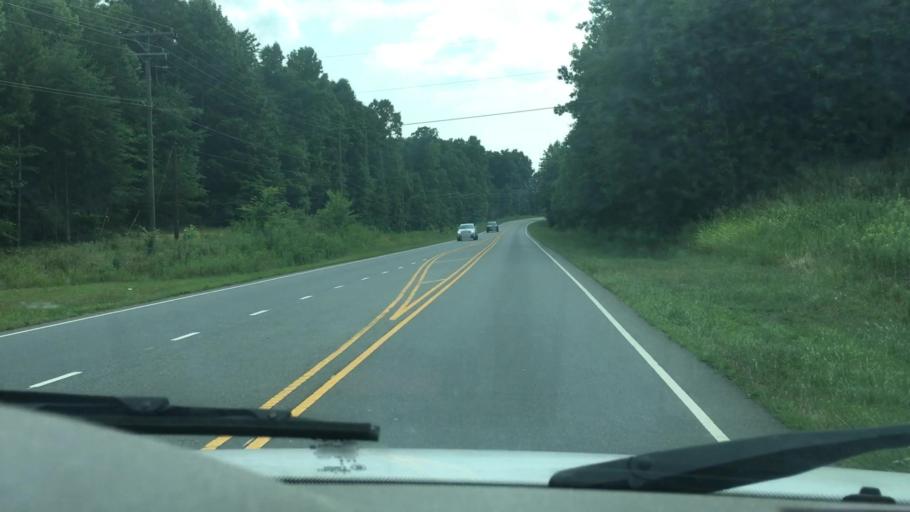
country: US
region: North Carolina
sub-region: Mecklenburg County
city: Huntersville
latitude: 35.4437
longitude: -80.8366
